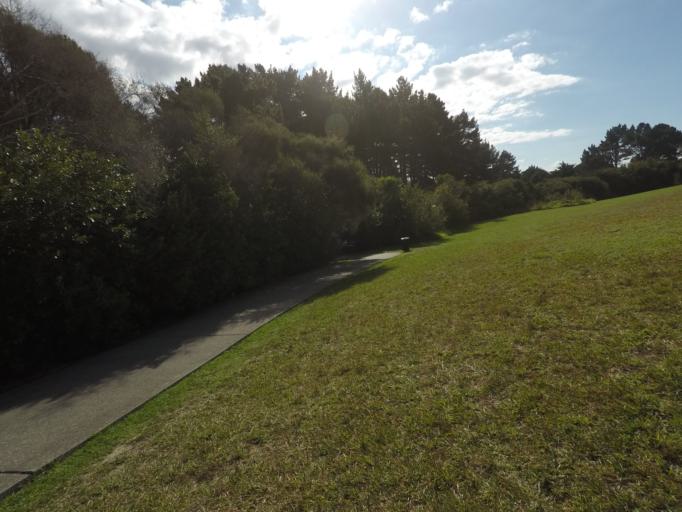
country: NZ
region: Auckland
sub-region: Auckland
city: Rosebank
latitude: -36.8863
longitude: 174.6967
